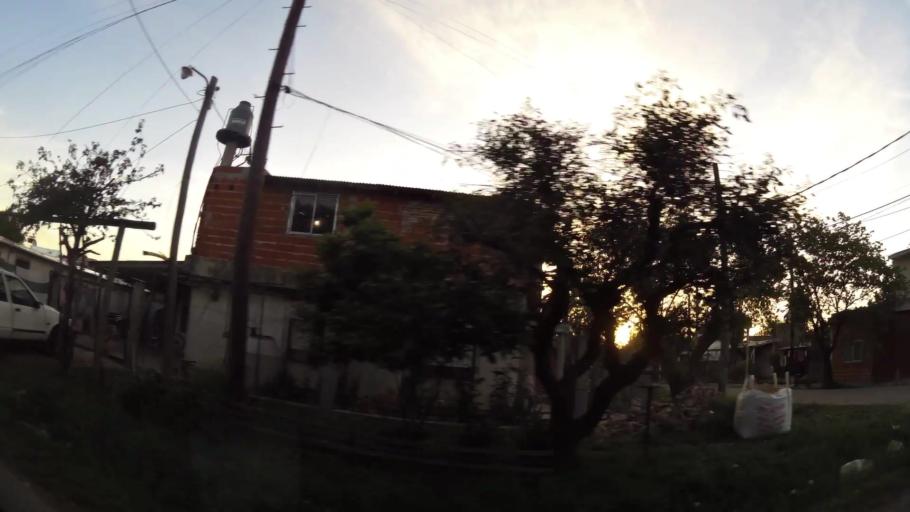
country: AR
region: Buenos Aires
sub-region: Partido de Quilmes
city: Quilmes
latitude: -34.7858
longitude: -58.2256
